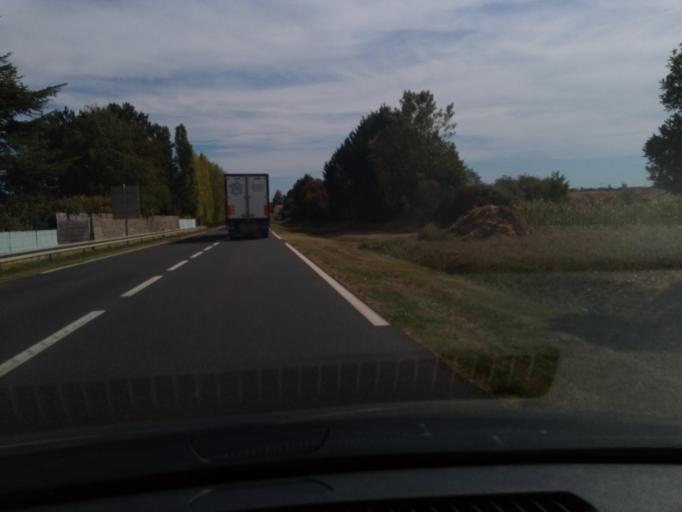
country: FR
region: Poitou-Charentes
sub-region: Departement de la Vienne
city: Terce
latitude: 46.4816
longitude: 0.5148
